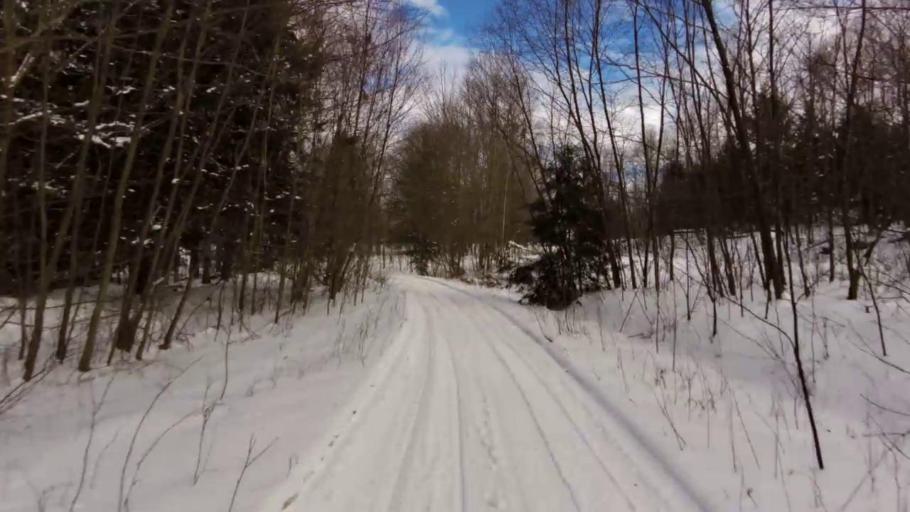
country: US
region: Pennsylvania
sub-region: McKean County
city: Foster Brook
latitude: 42.0106
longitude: -78.5617
